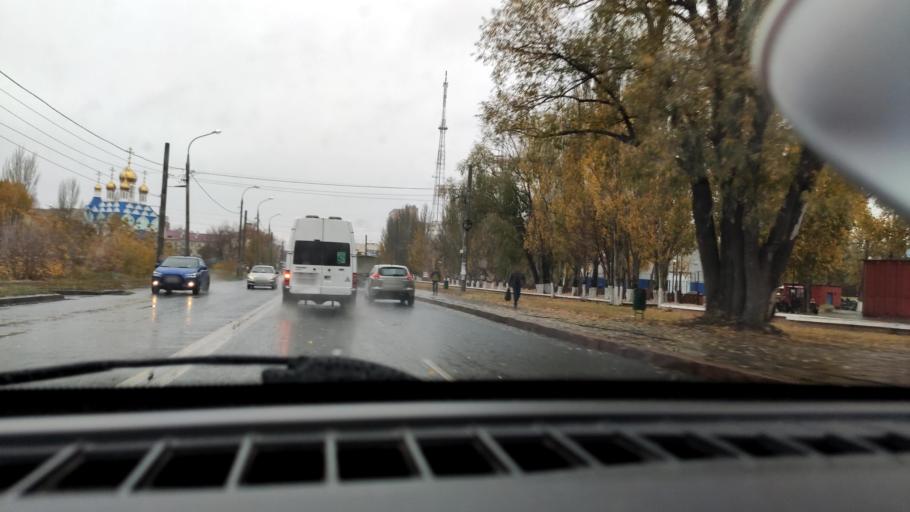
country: RU
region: Samara
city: Samara
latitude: 53.2261
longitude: 50.1972
